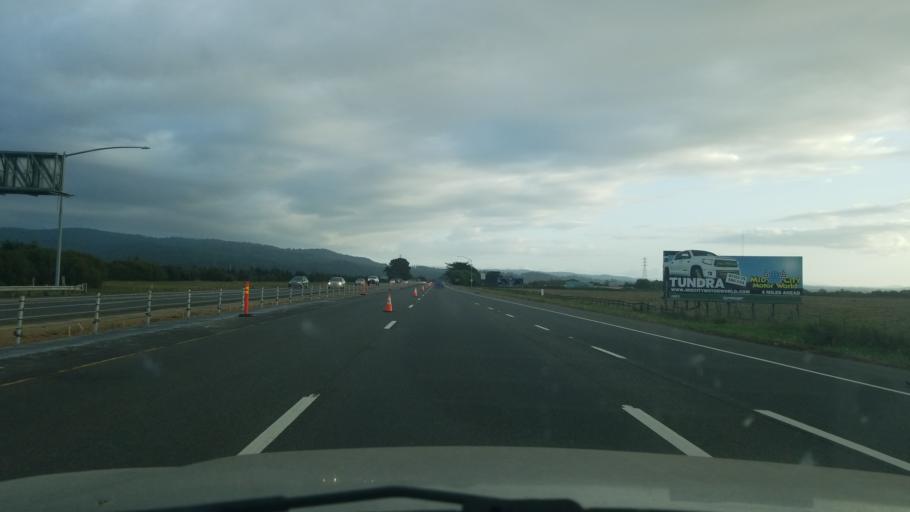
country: US
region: California
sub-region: Humboldt County
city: Arcata
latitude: 40.8585
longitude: -124.0826
